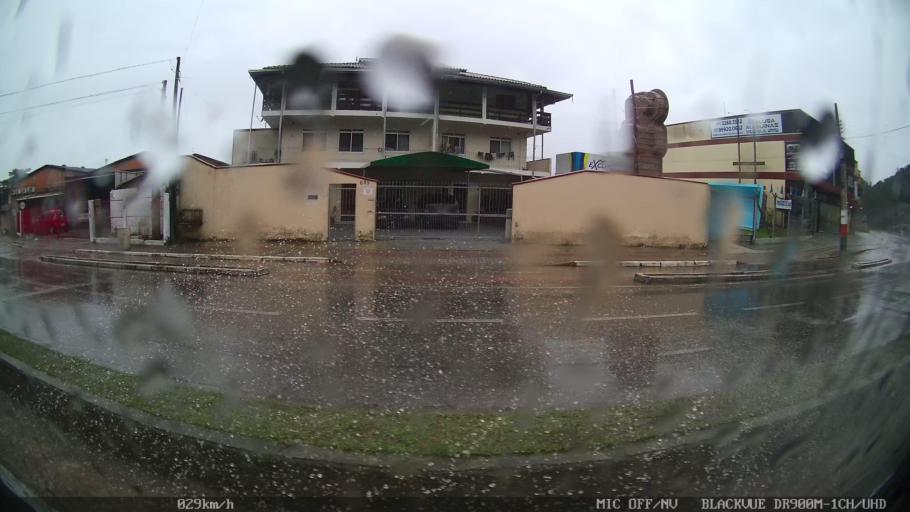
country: BR
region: Santa Catarina
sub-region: Balneario Camboriu
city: Balneario Camboriu
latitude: -27.0081
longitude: -48.6488
